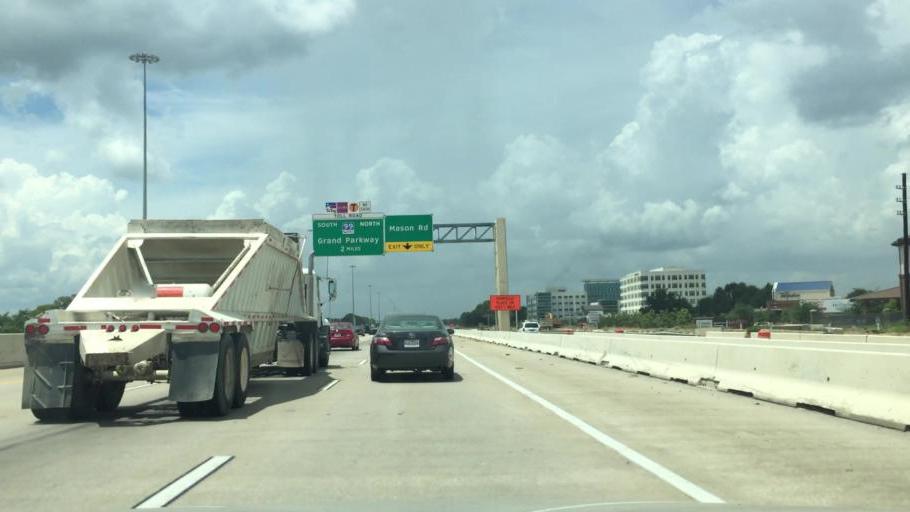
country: US
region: Texas
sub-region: Harris County
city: Cypress
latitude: 29.9824
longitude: -95.7272
